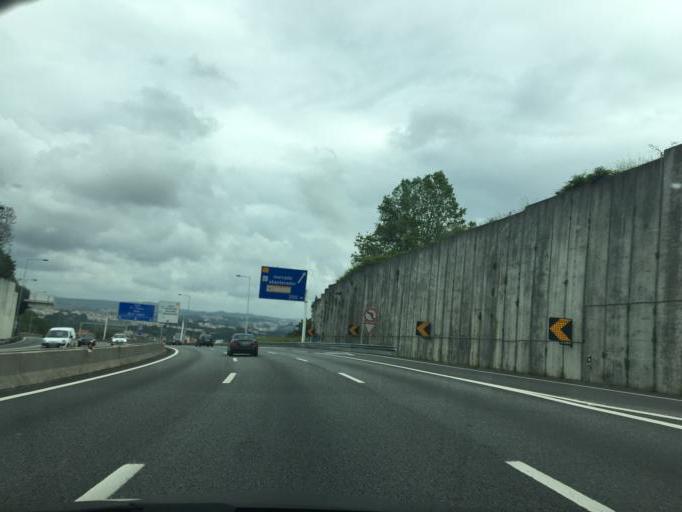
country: PT
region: Porto
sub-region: Maia
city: Pedroucos
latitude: 41.1669
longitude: -8.5867
